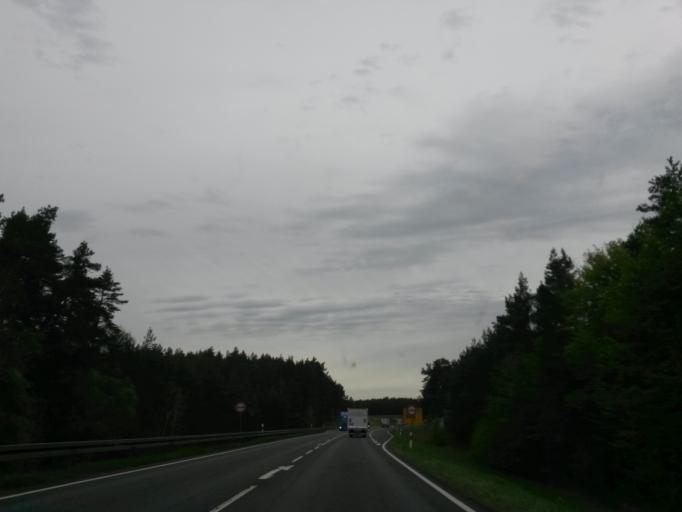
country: DE
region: Bavaria
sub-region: Upper Franconia
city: Pommersfelden
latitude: 49.7400
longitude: 10.8270
